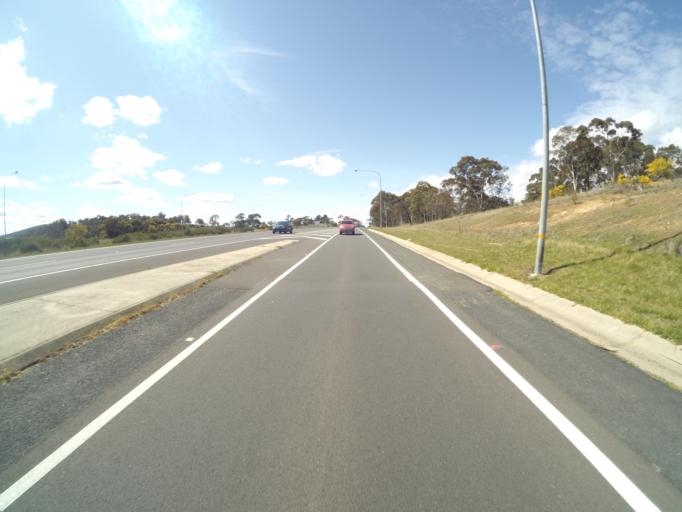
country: AU
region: New South Wales
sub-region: Goulburn Mulwaree
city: Goulburn
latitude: -34.7394
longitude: 149.7784
